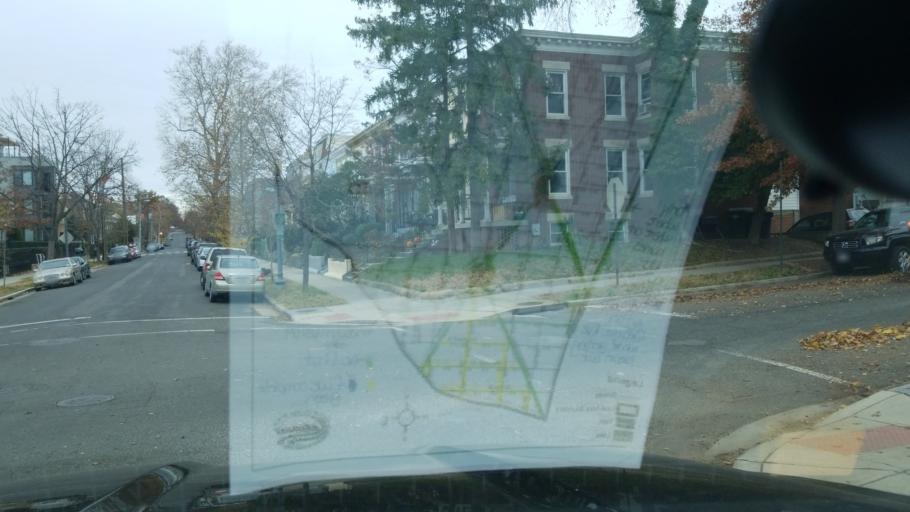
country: US
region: Maryland
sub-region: Prince George's County
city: Chillum
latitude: 38.9408
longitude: -77.0233
